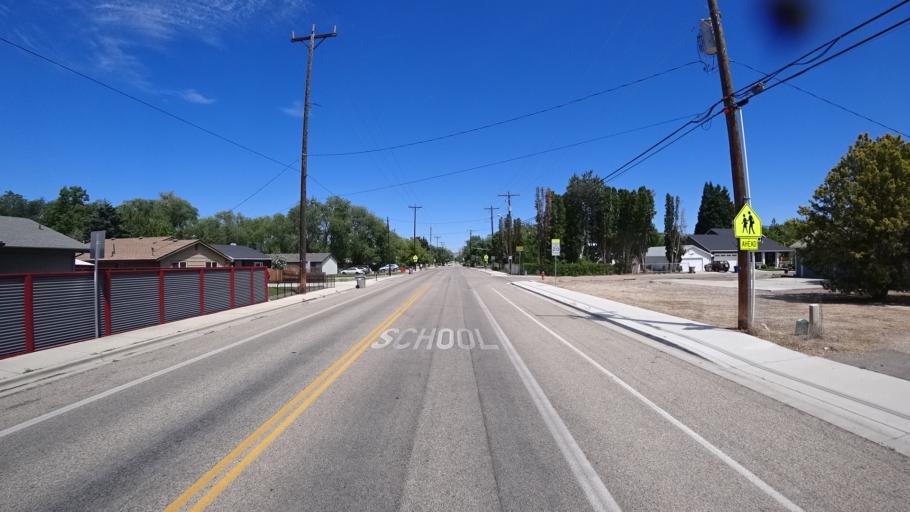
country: US
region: Idaho
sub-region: Ada County
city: Garden City
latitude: 43.5960
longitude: -116.2335
